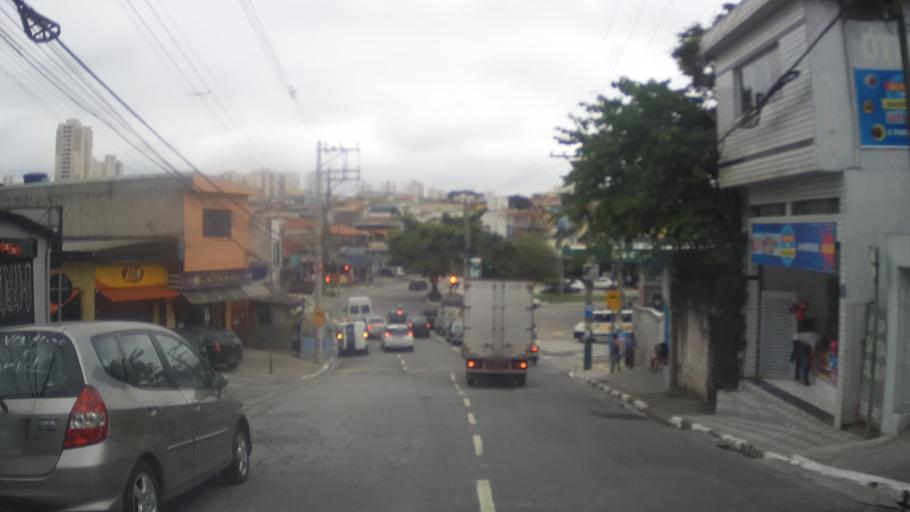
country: BR
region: Sao Paulo
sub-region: Guarulhos
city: Guarulhos
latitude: -23.4372
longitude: -46.5472
